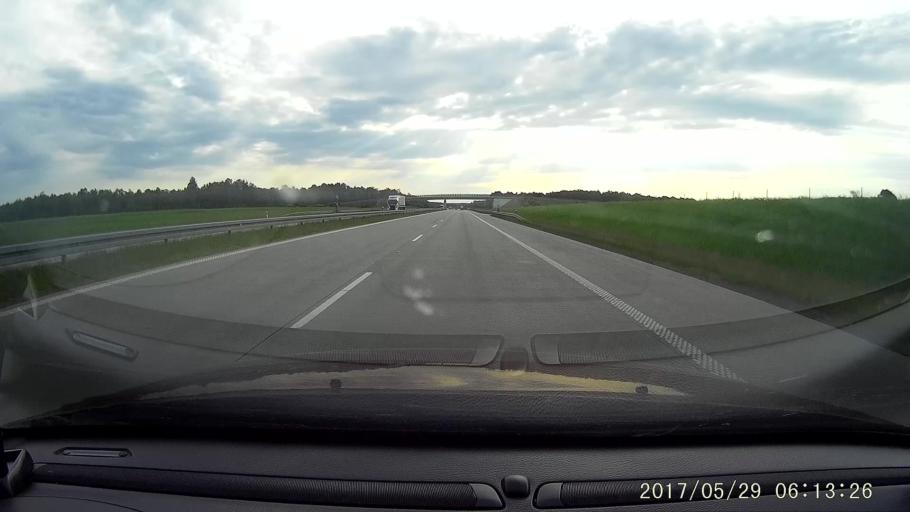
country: PL
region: Lower Silesian Voivodeship
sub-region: Powiat zgorzelecki
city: Wegliniec
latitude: 51.2275
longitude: 15.3034
